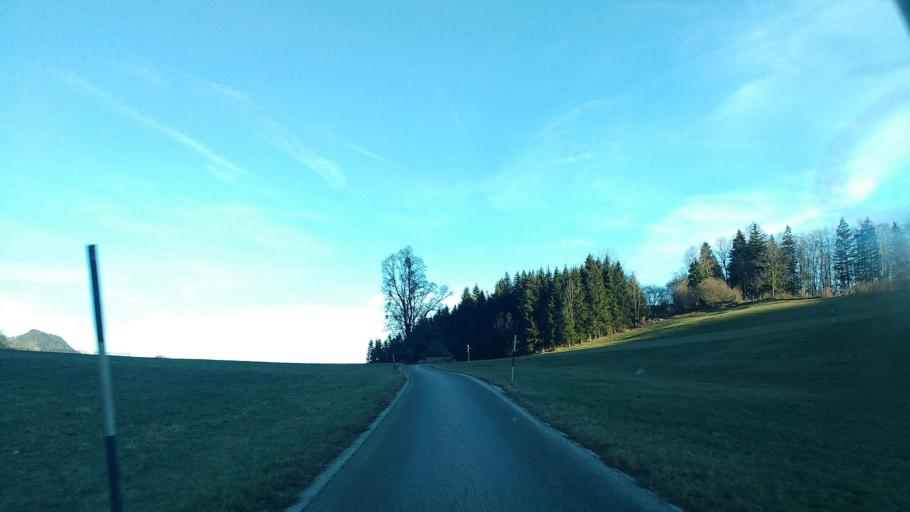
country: AT
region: Upper Austria
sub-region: Politischer Bezirk Kirchdorf an der Krems
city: Micheldorf in Oberoesterreich
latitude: 47.8972
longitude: 14.2114
